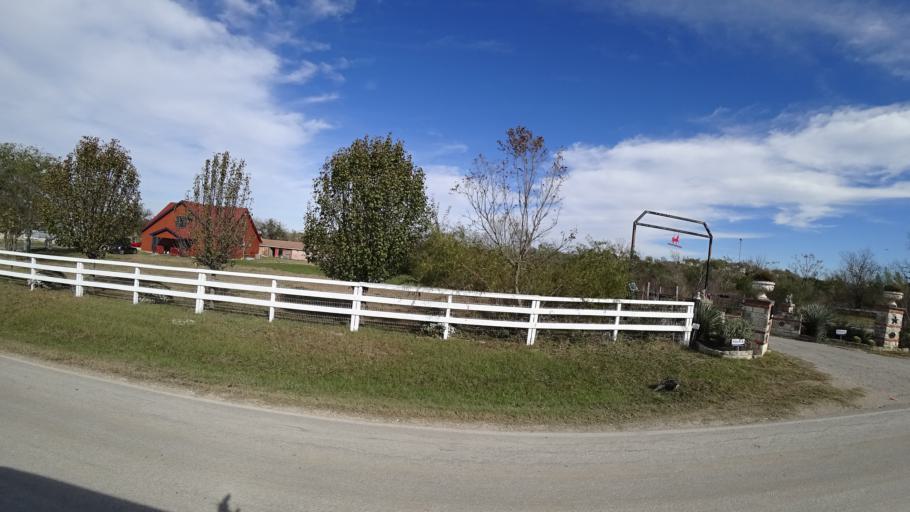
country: US
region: Texas
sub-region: Travis County
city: Onion Creek
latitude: 30.1176
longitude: -97.7504
